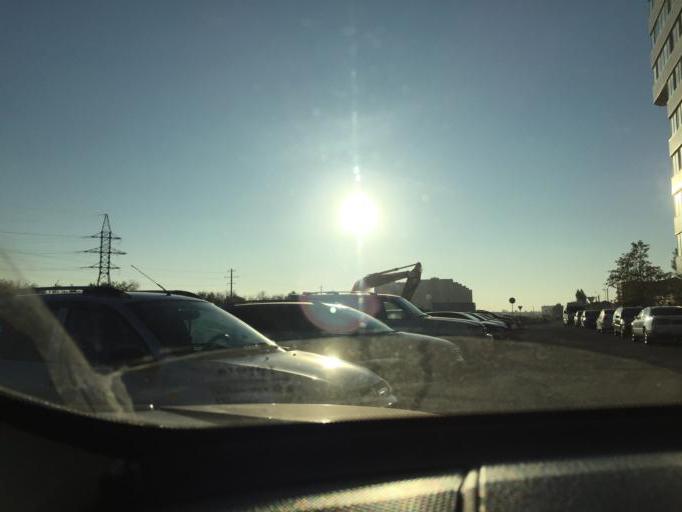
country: KZ
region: Astana Qalasy
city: Astana
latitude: 51.1574
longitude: 71.5116
